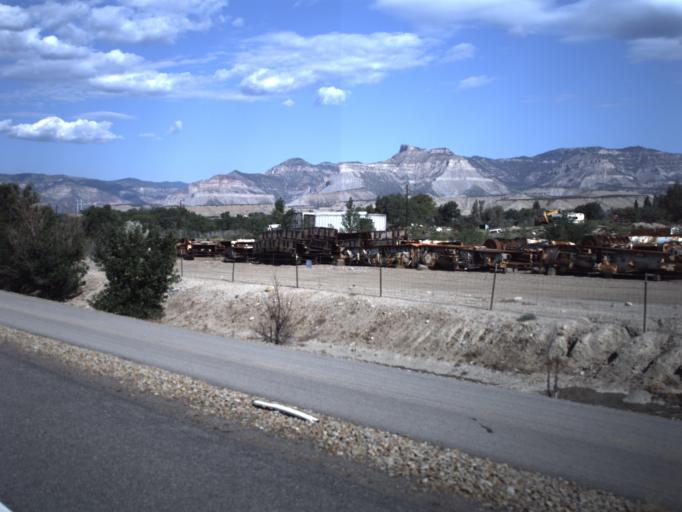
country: US
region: Utah
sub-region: Emery County
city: Huntington
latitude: 39.3394
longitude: -110.9580
